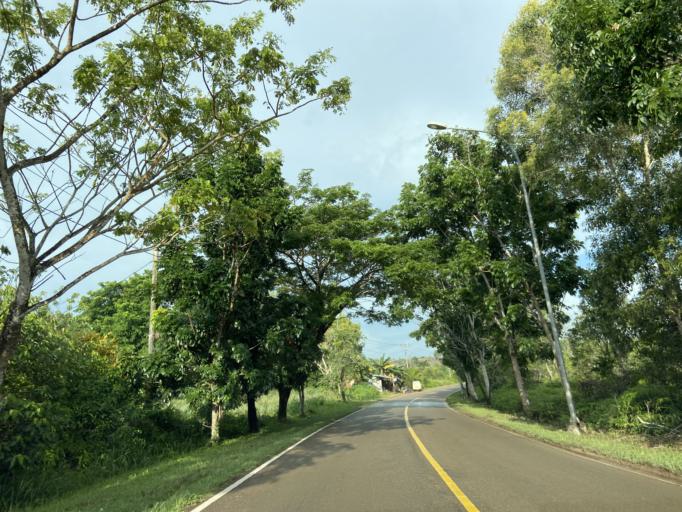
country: ID
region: Riau Islands
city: Tanjungpinang
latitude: 0.9453
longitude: 104.0626
